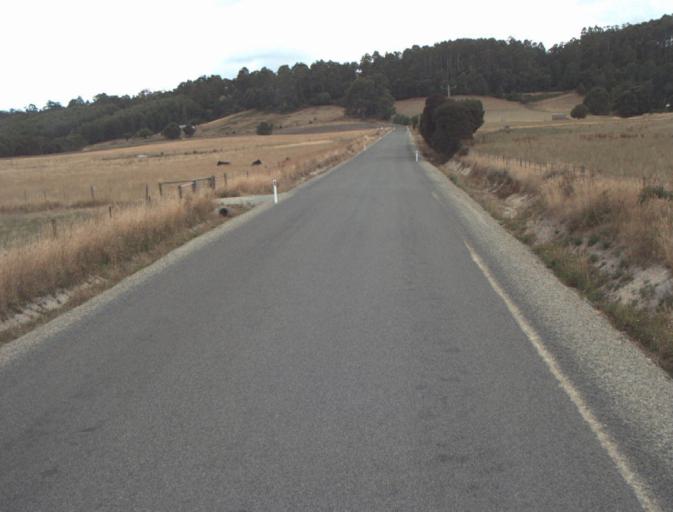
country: AU
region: Tasmania
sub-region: Launceston
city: Mayfield
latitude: -41.2056
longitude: 147.1884
